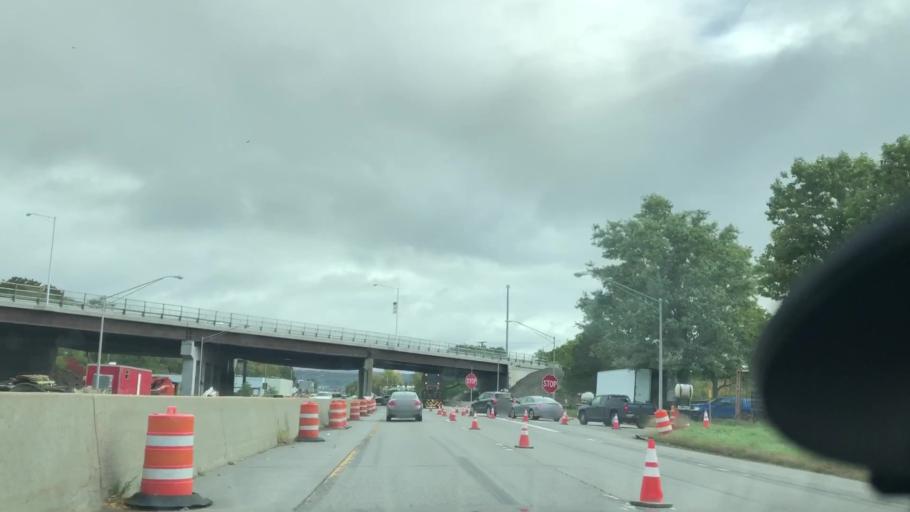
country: US
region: New York
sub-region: Oneida County
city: Yorkville
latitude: 43.0917
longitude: -75.2650
